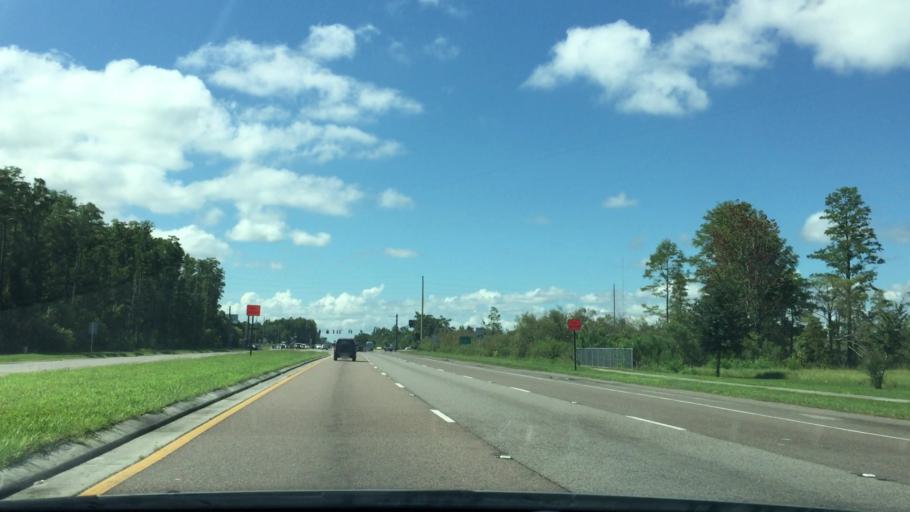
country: US
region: Florida
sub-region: Orange County
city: Hunters Creek
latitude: 28.3402
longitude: -81.4038
